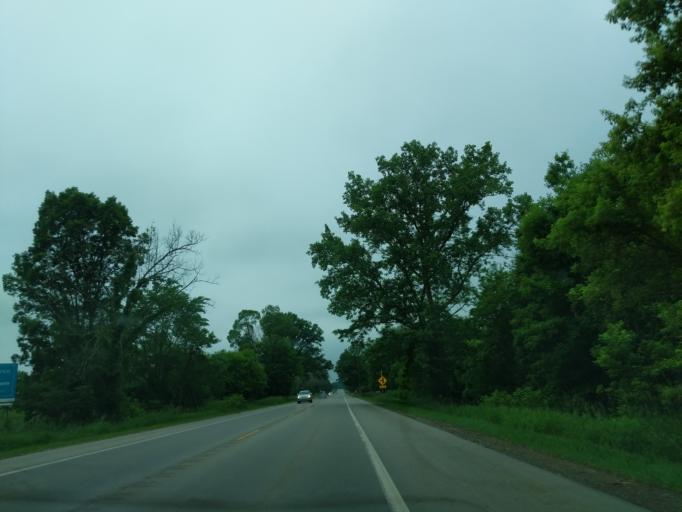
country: US
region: Michigan
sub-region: Branch County
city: Quincy
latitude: 41.9489
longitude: -84.8429
